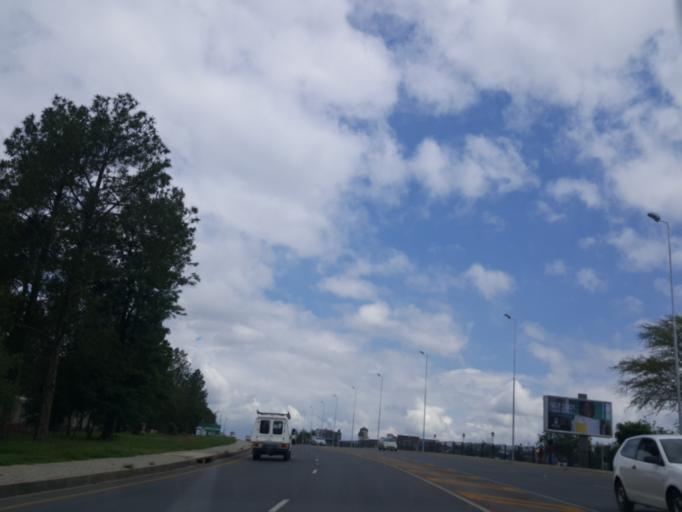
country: ZA
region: Gauteng
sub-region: City of Johannesburg Metropolitan Municipality
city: Diepsloot
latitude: -25.9978
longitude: 27.9829
